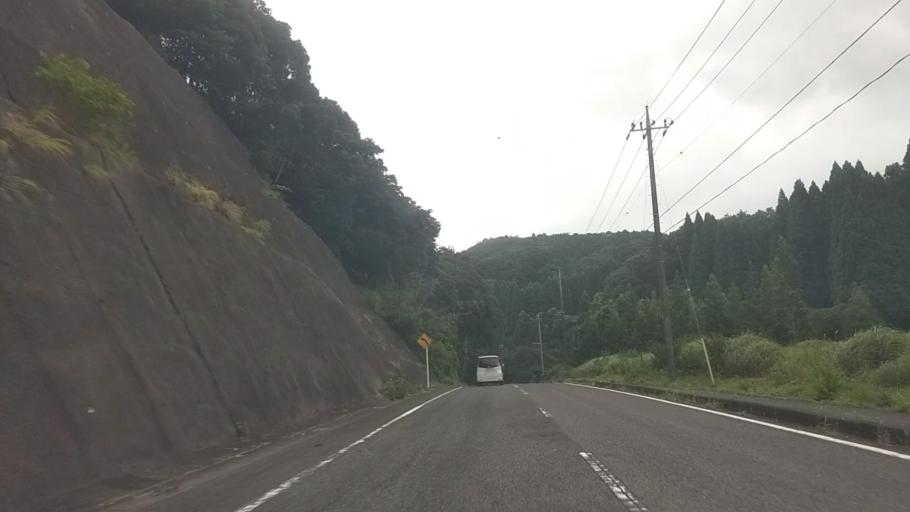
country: JP
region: Chiba
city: Kawaguchi
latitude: 35.2438
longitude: 140.1801
